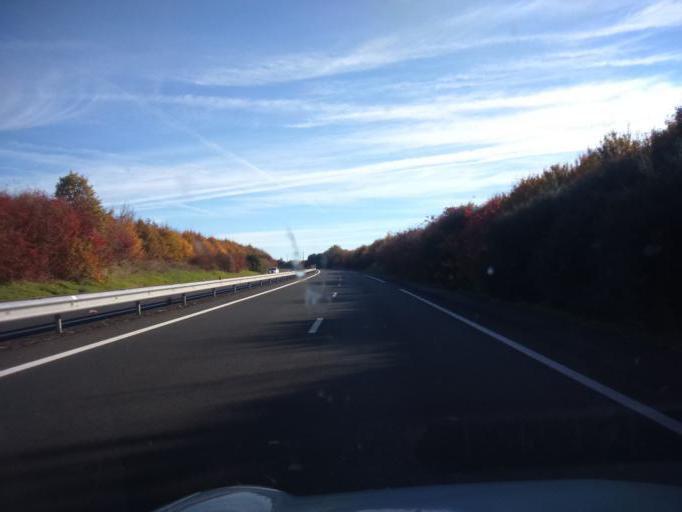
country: FR
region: Poitou-Charentes
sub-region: Departement de la Charente-Maritime
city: Tonnay-Charente
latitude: 45.9544
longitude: -0.8968
